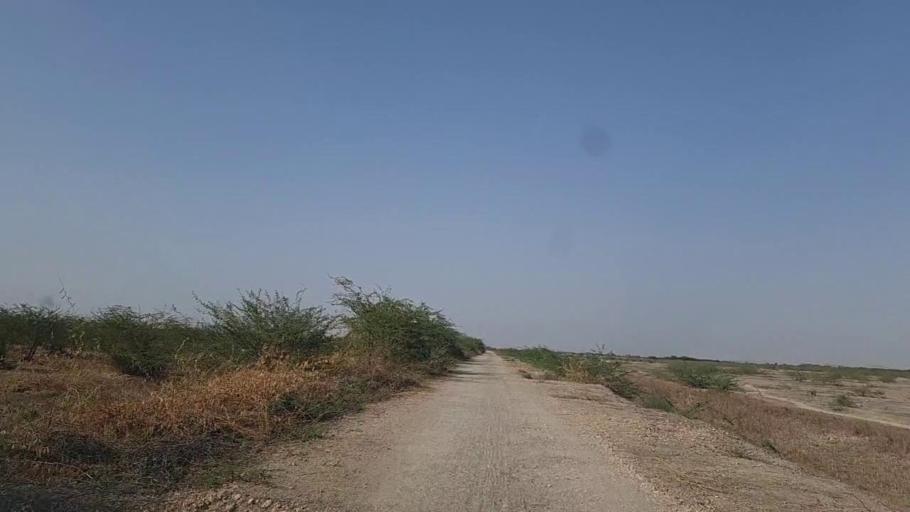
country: PK
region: Sindh
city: Naukot
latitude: 24.6043
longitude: 69.2747
